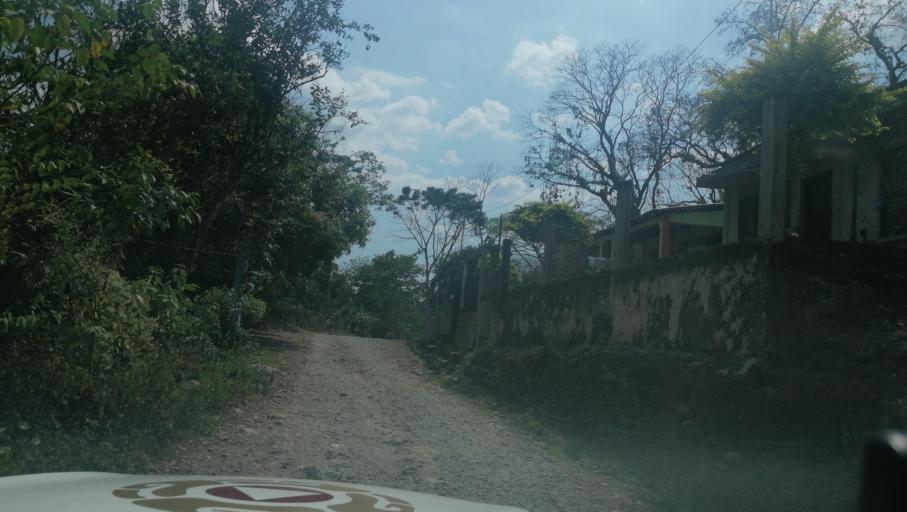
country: MX
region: Chiapas
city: Veinte de Noviembre
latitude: 15.0172
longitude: -92.2417
